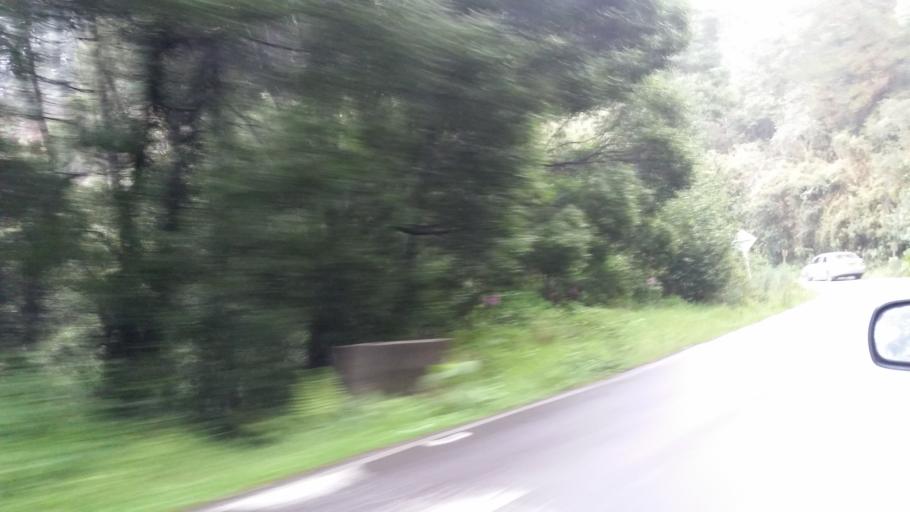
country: CO
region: Bogota D.C.
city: Bogota
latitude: 4.5955
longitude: -74.0559
